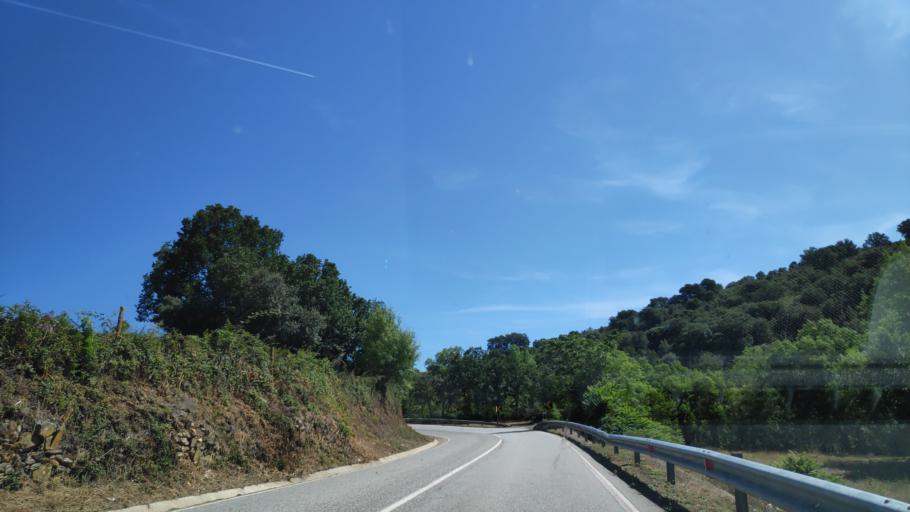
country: PT
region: Braganca
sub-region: Braganca Municipality
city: Braganca
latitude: 41.8854
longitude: -6.7360
